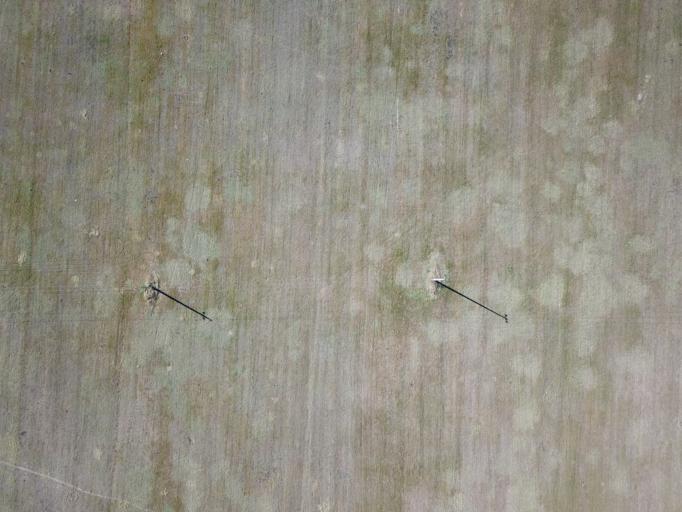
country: HU
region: Pest
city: Budakalasz
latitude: 47.6106
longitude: 19.0685
